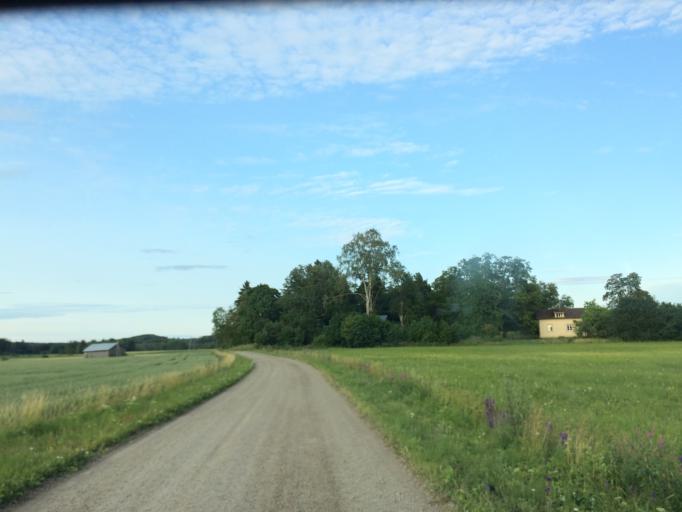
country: FI
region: Haeme
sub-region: Haemeenlinna
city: Janakkala
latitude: 60.8771
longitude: 24.6242
